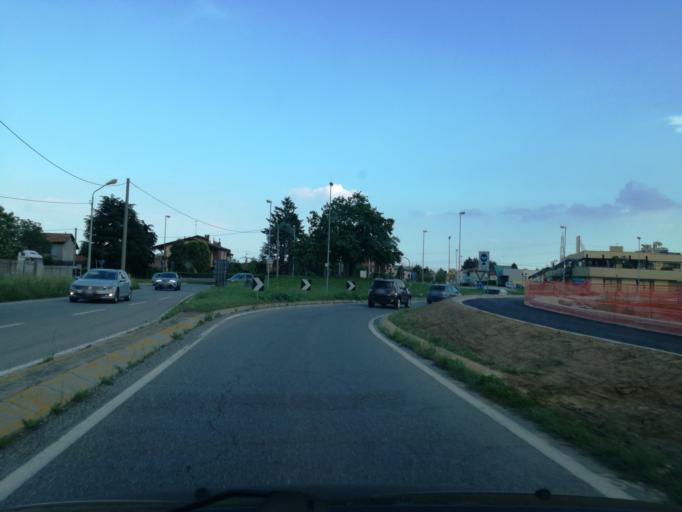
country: IT
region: Lombardy
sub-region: Provincia di Monza e Brianza
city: Cornate d'Adda
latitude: 45.6398
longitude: 9.4701
